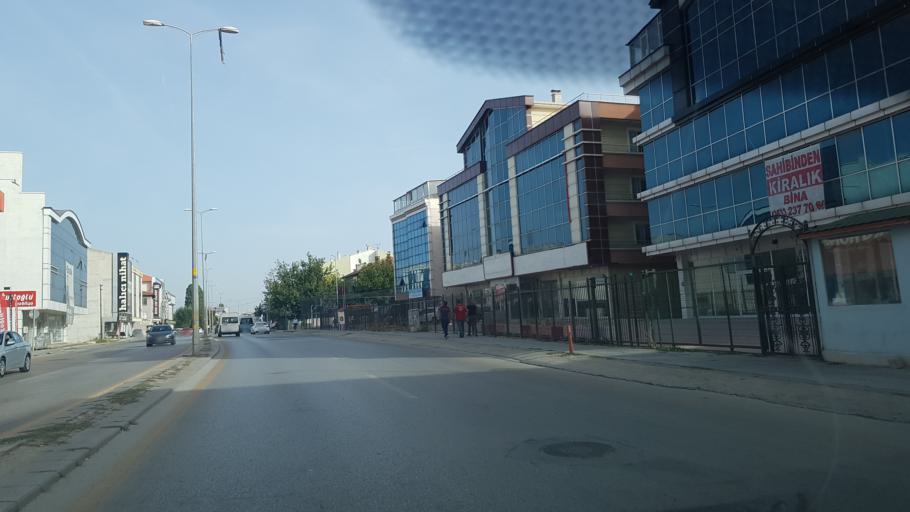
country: TR
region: Ankara
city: Etimesgut
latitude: 39.9522
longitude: 32.6448
